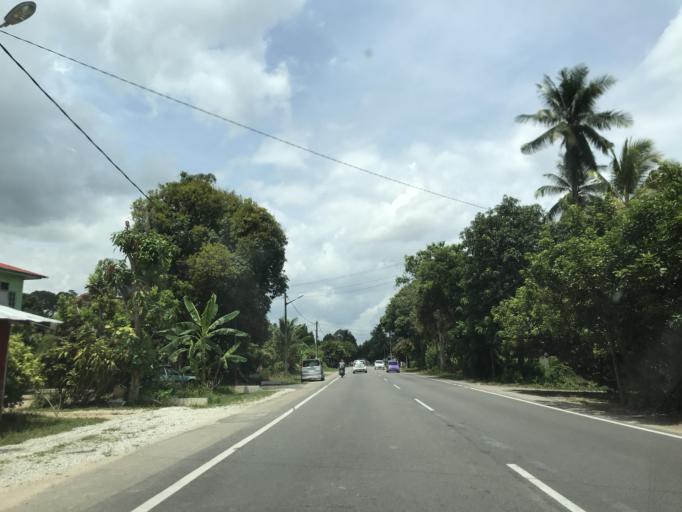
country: MY
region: Kelantan
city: Kota Bharu
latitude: 6.0919
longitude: 102.2081
